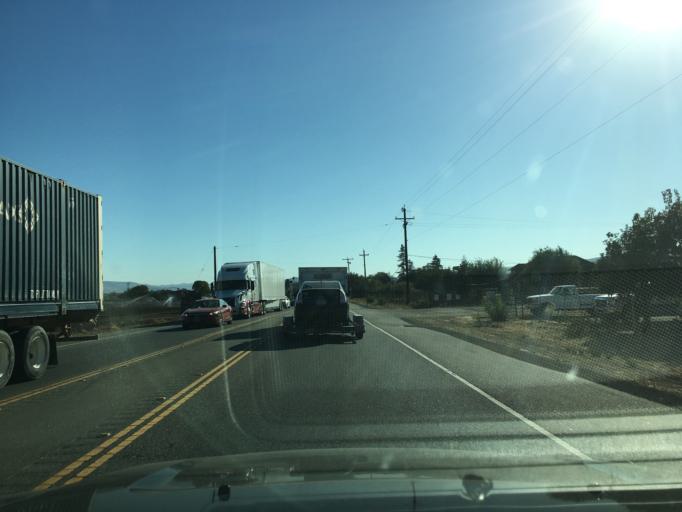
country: US
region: California
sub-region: Santa Clara County
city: Gilroy
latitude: 37.0089
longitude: -121.5173
